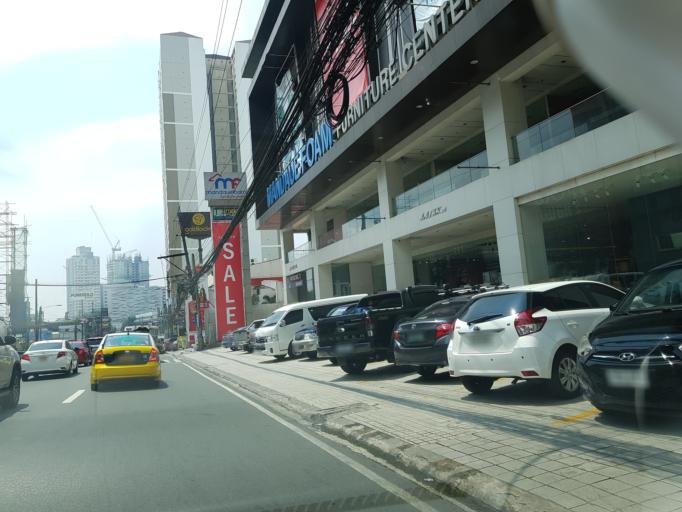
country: PH
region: Metro Manila
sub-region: Mandaluyong
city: Mandaluyong City
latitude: 14.5881
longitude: 121.0446
